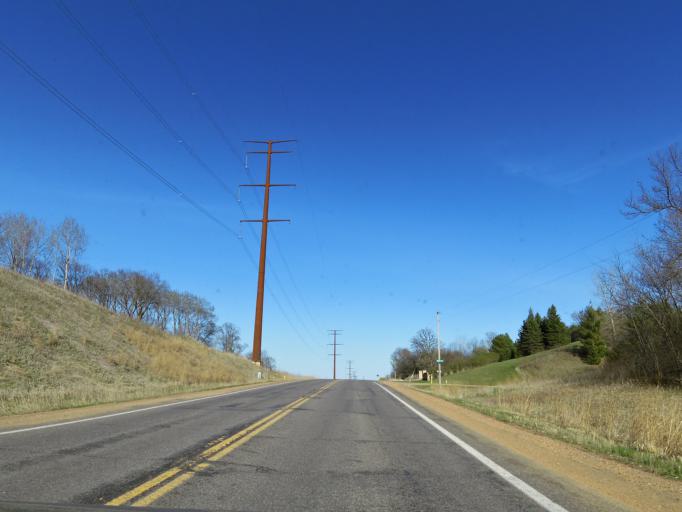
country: US
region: Minnesota
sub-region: Rice County
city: Lonsdale
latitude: 44.5727
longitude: -93.4516
